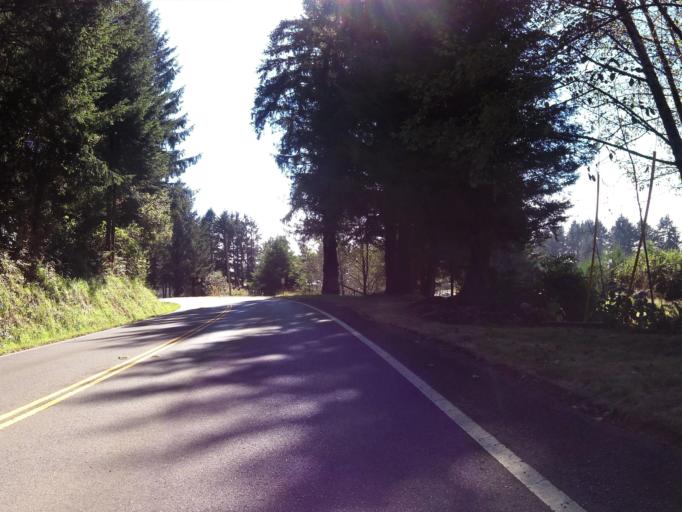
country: US
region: Oregon
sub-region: Curry County
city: Harbor
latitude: 41.9545
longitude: -124.2023
